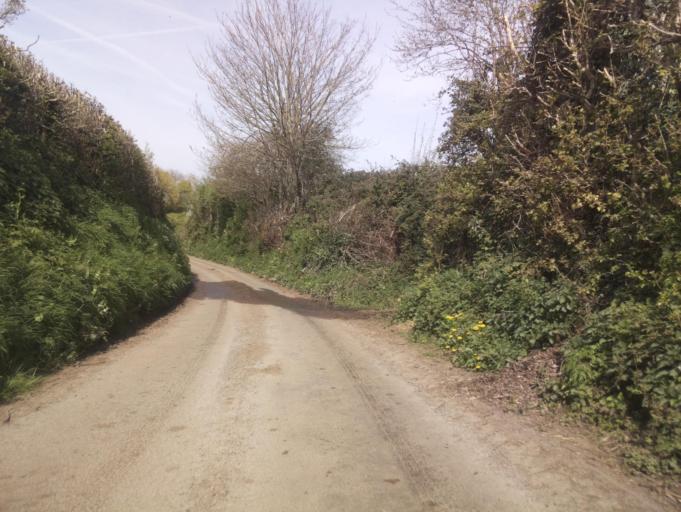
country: GB
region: England
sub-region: Dorset
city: Sherborne
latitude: 50.9913
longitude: -2.5418
